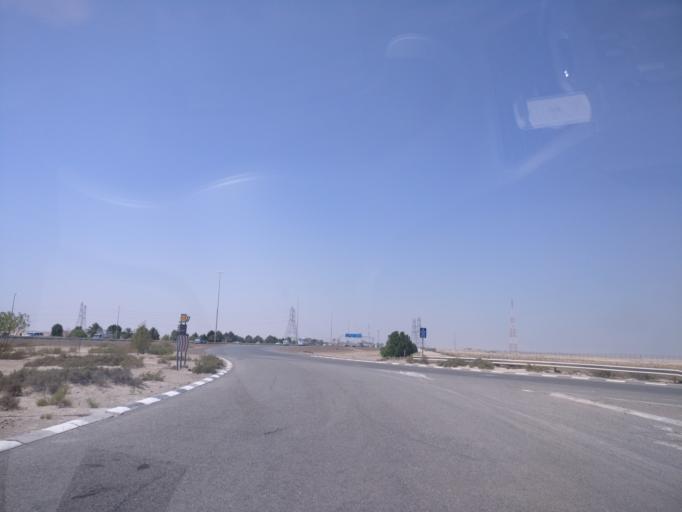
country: AE
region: Dubai
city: Dubai
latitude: 24.9074
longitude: 54.9502
